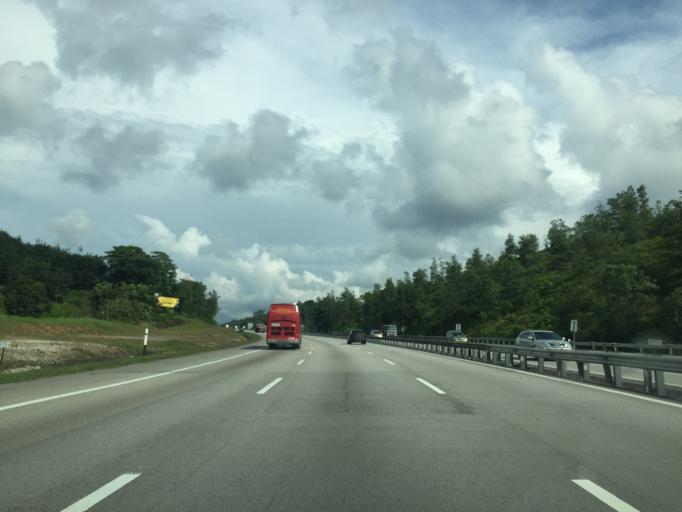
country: MY
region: Selangor
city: Serendah
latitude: 3.5135
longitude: 101.5280
